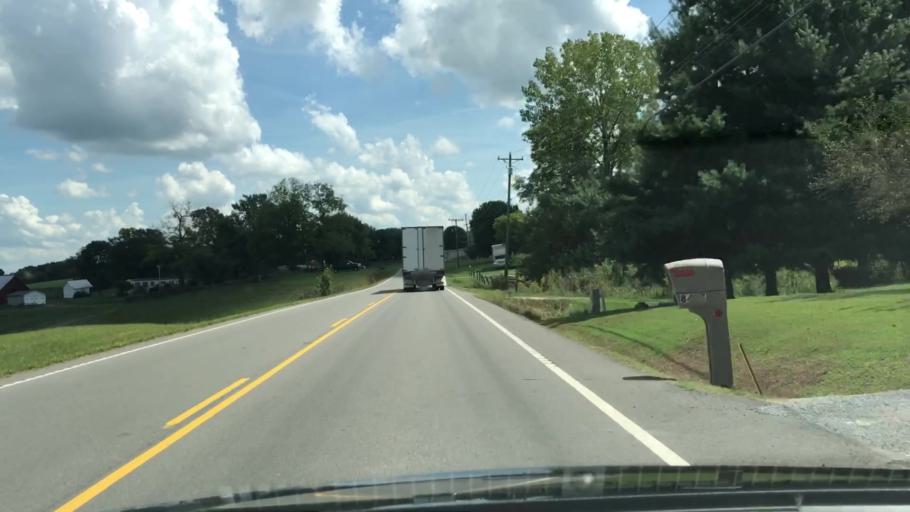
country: US
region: Tennessee
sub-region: Robertson County
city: Cross Plains
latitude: 36.5355
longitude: -86.6550
